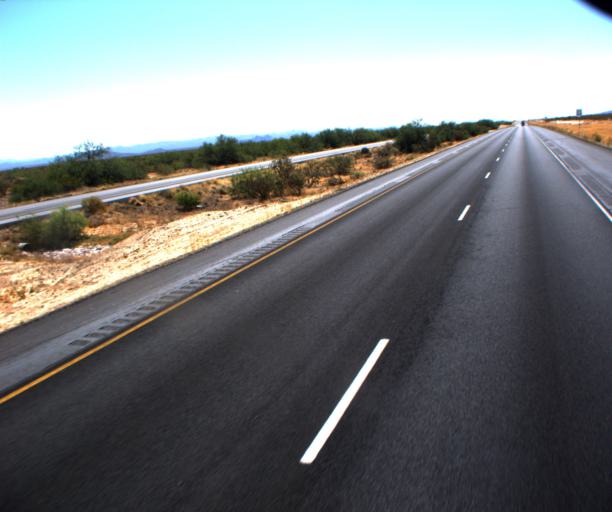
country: US
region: Arizona
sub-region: Yavapai County
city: Congress
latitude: 34.0676
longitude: -112.8709
